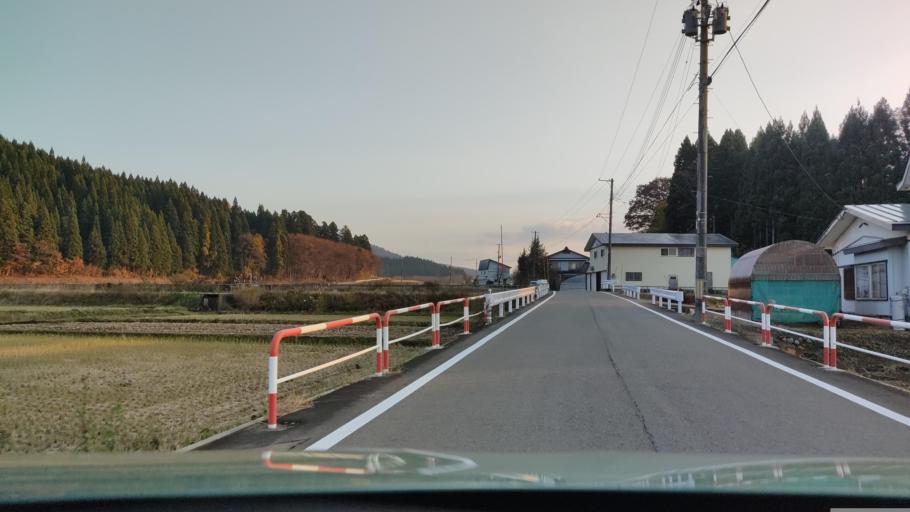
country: JP
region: Akita
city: Omagari
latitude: 39.4243
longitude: 140.5839
